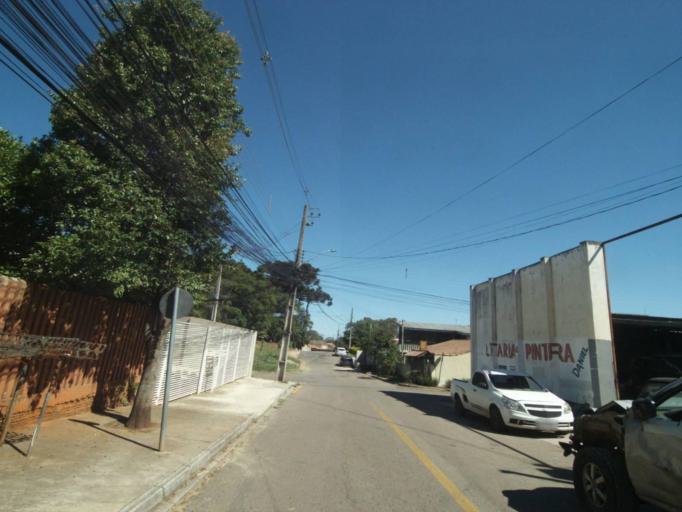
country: BR
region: Parana
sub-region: Curitiba
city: Curitiba
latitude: -25.4614
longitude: -49.3496
